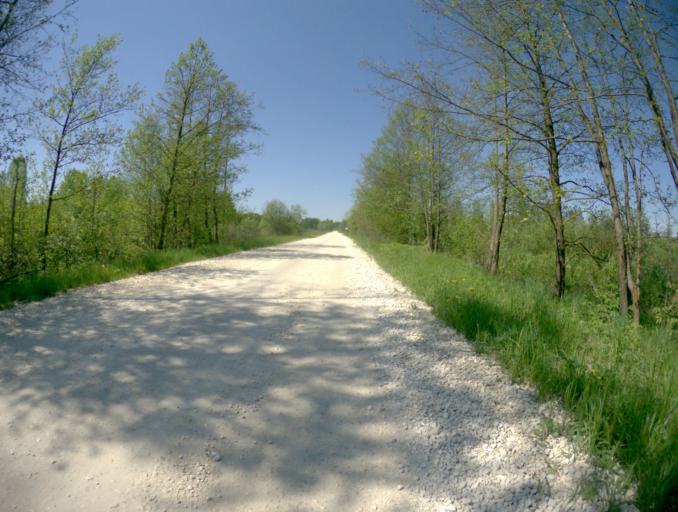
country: RU
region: Vladimir
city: Anopino
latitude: 55.7087
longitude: 40.6311
